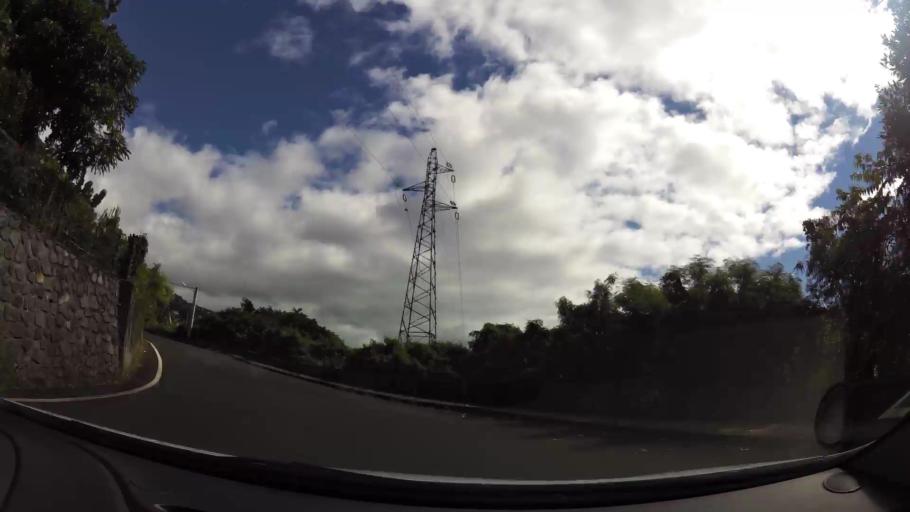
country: RE
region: Reunion
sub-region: Reunion
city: Saint-Denis
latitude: -20.9299
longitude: 55.4939
